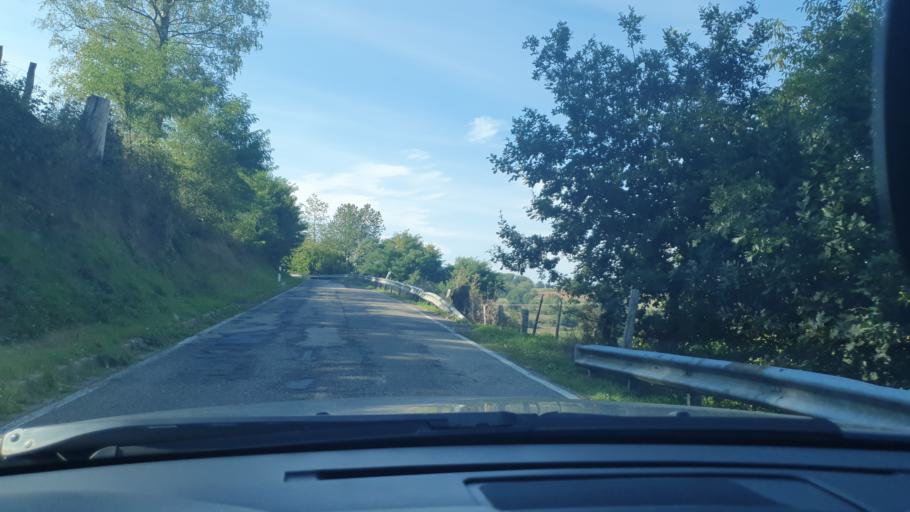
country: DE
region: Rheinland-Pfalz
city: Battweiler
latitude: 49.2928
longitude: 7.4624
